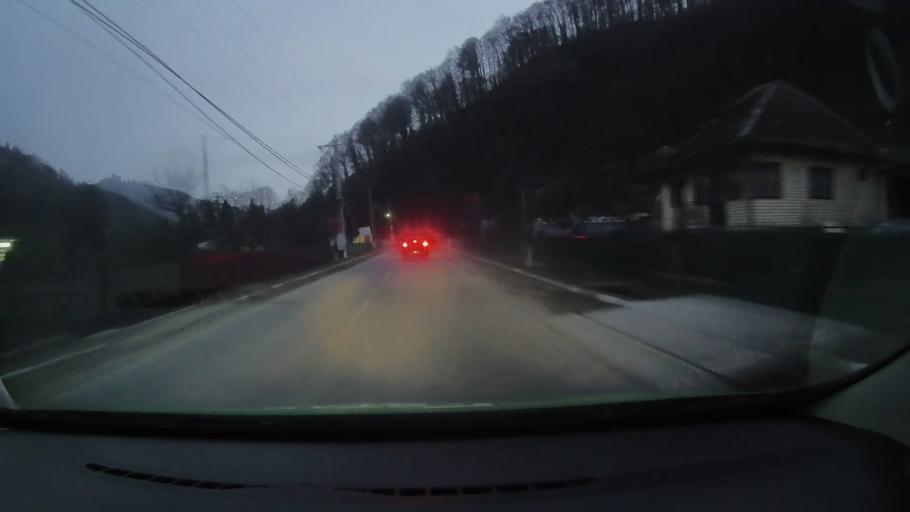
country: RO
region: Prahova
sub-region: Comuna Valea Doftanei
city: Tesila
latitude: 45.2835
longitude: 25.7237
